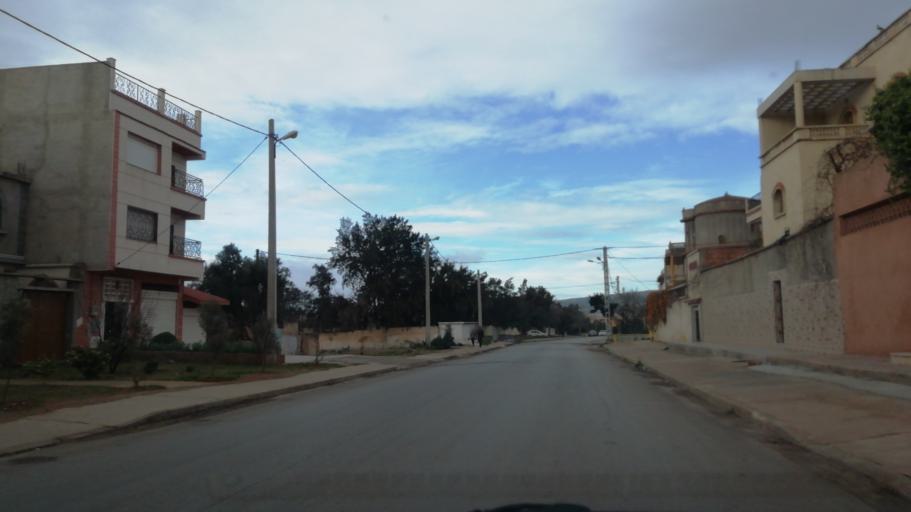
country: DZ
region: Oran
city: Oran
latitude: 35.6921
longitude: -0.6028
